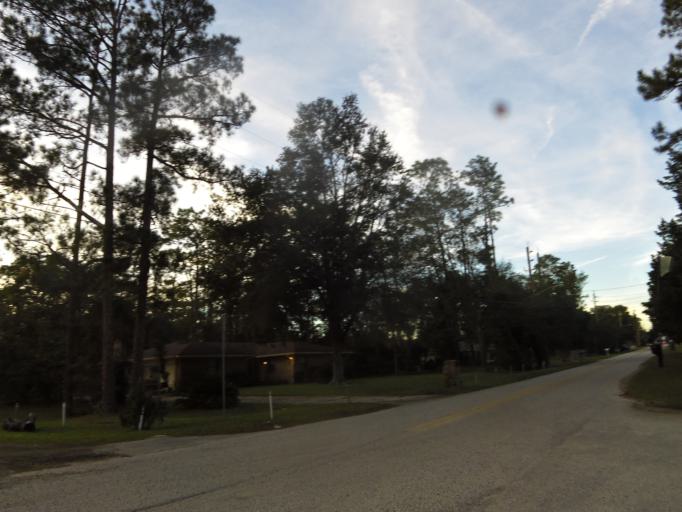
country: US
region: Florida
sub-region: Saint Johns County
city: Fruit Cove
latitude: 30.1581
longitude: -81.5424
